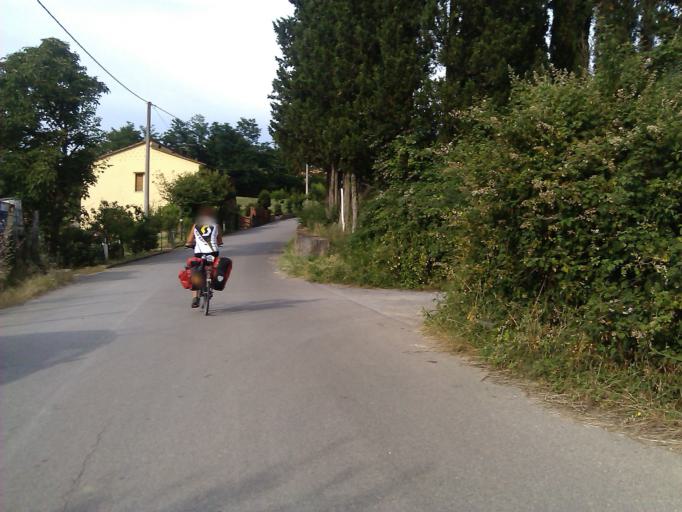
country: IT
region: Tuscany
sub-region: Province of Arezzo
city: Bucine
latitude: 43.4969
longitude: 11.6272
